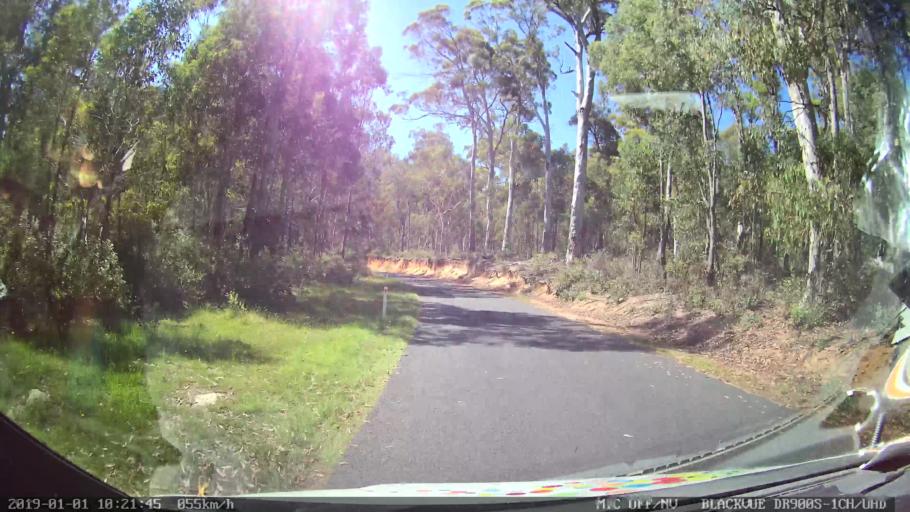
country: AU
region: New South Wales
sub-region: Snowy River
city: Jindabyne
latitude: -36.0776
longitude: 148.1973
